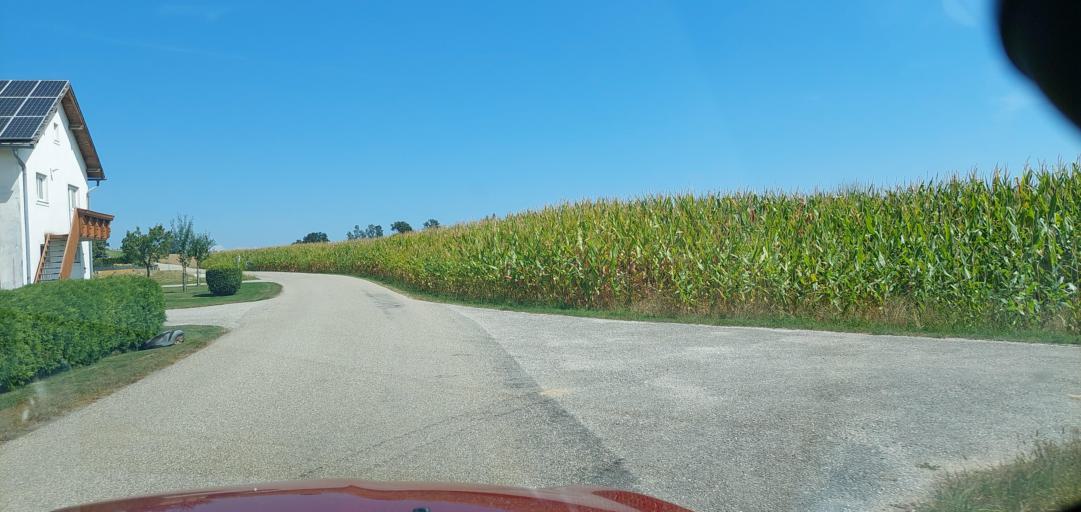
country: AT
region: Upper Austria
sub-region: Wels-Land
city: Offenhausen
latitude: 48.1376
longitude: 13.8331
